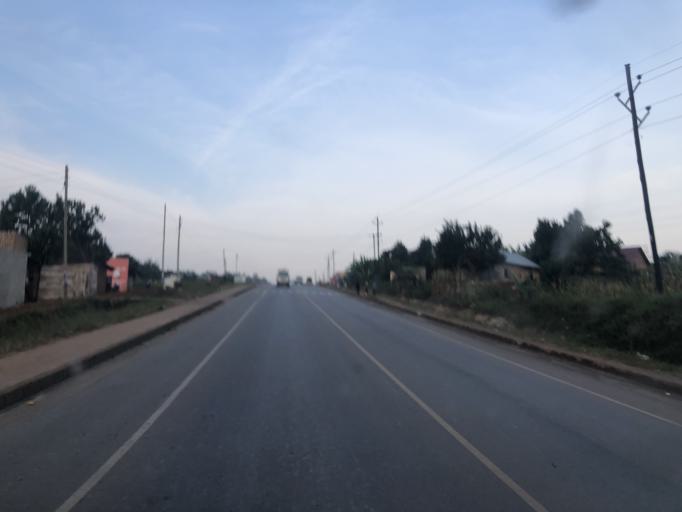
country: UG
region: Central Region
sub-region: Mpigi District
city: Mpigi
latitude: 0.2426
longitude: 32.3639
